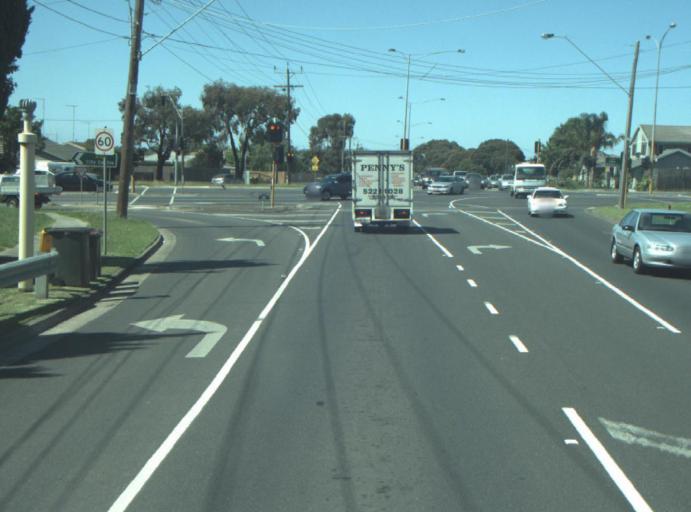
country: AU
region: Victoria
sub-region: Greater Geelong
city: Breakwater
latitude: -38.1817
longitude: 144.3450
